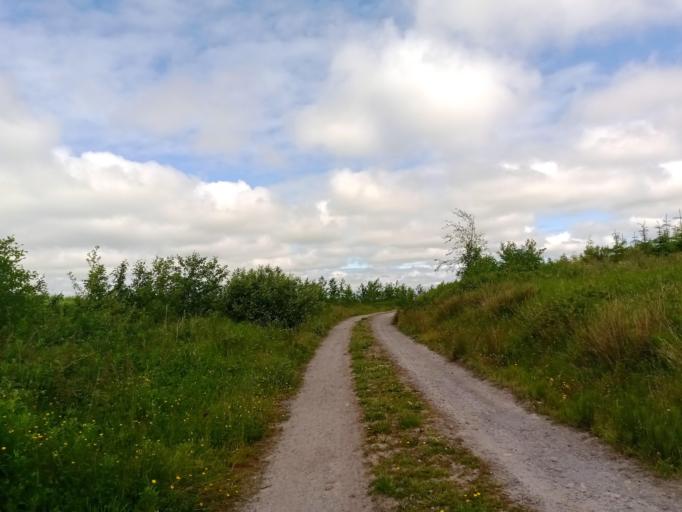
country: IE
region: Leinster
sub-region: Kilkenny
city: Ballyragget
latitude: 52.7919
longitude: -7.4454
